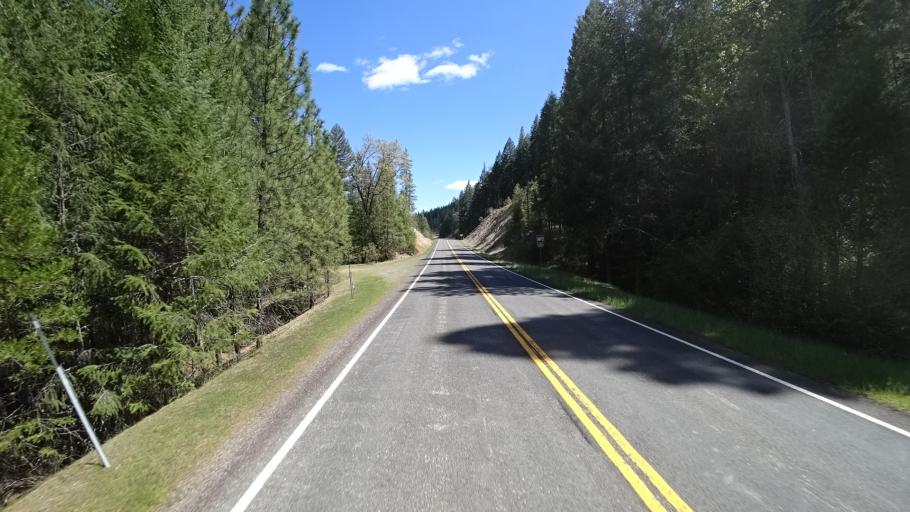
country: US
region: California
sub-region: Trinity County
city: Weaverville
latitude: 40.8467
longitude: -122.8638
